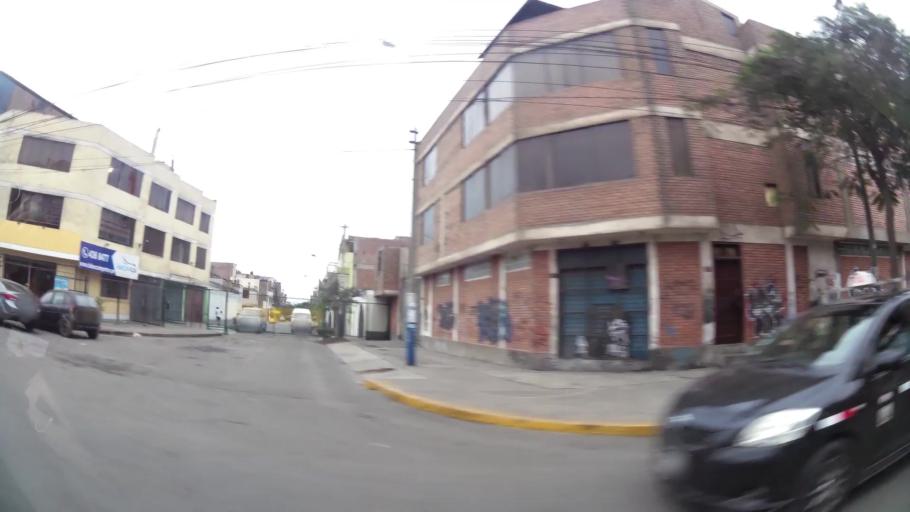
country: PE
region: Lima
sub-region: Lima
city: San Luis
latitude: -12.0726
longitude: -76.9819
